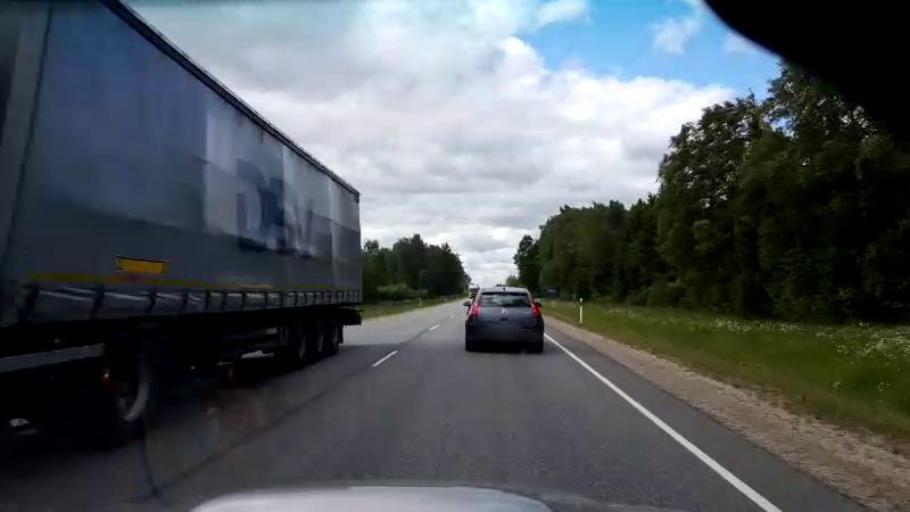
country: EE
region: Raplamaa
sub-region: Maerjamaa vald
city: Marjamaa
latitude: 58.9368
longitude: 24.4645
